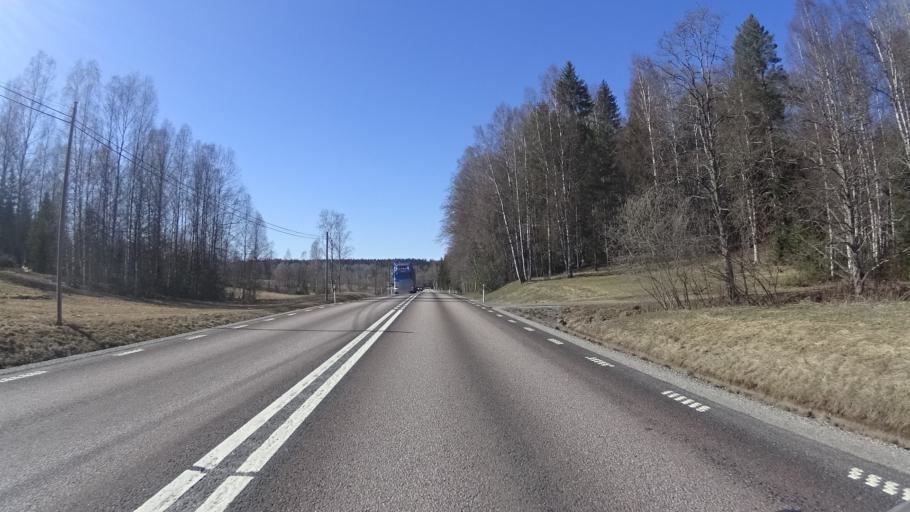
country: SE
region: Vaermland
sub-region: Sunne Kommun
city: Sunne
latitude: 59.6649
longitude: 12.9164
